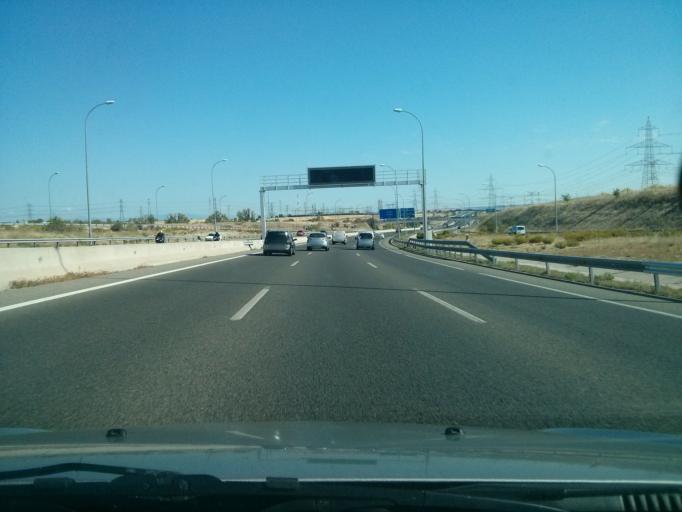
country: ES
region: Madrid
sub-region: Provincia de Madrid
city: San Sebastian de los Reyes
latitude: 40.5535
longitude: -3.6065
